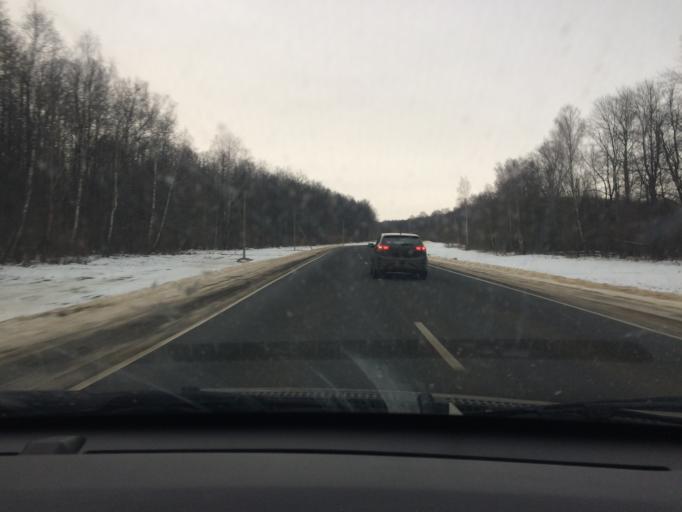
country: RU
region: Tula
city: Venev
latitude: 54.3370
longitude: 38.1228
